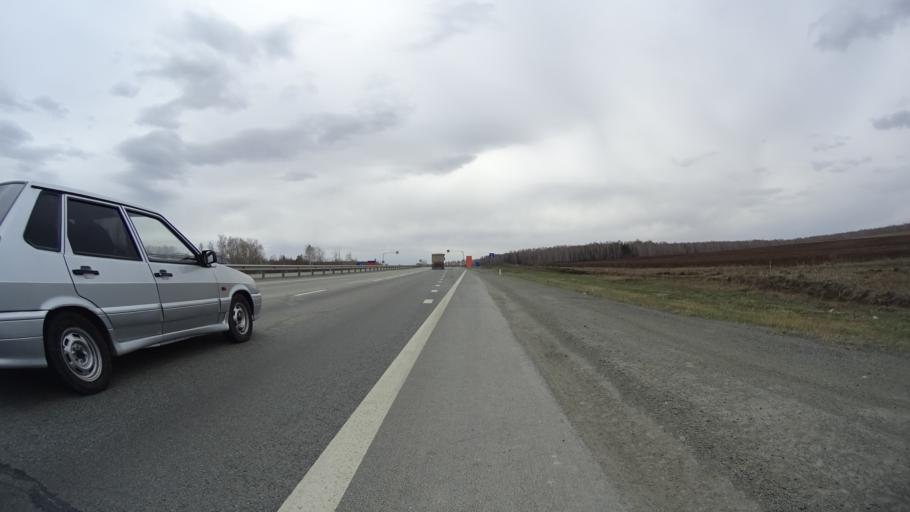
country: RU
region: Chelyabinsk
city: Yemanzhelinka
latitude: 54.8253
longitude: 61.3099
